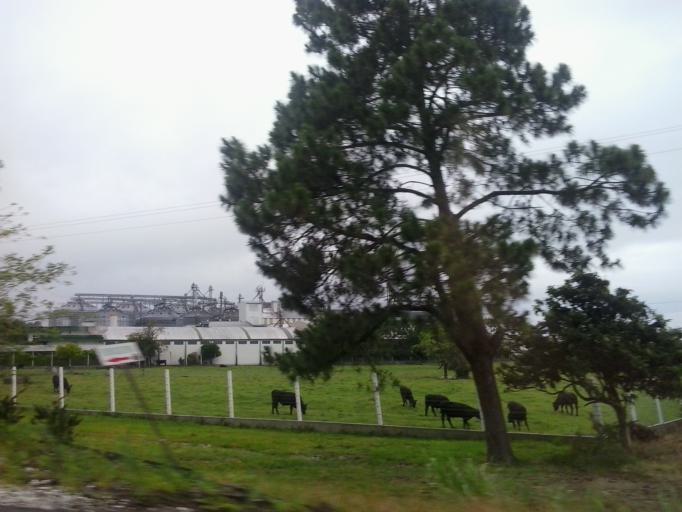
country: BR
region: Rio Grande do Sul
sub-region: Candelaria
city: Candelaria
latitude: -29.7149
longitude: -53.2509
